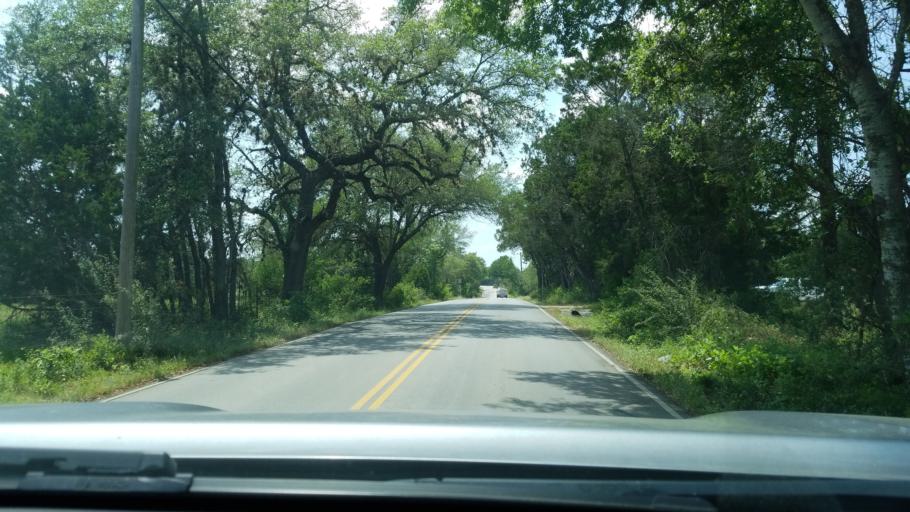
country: US
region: Texas
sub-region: Hays County
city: Woodcreek
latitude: 30.0293
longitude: -98.1248
